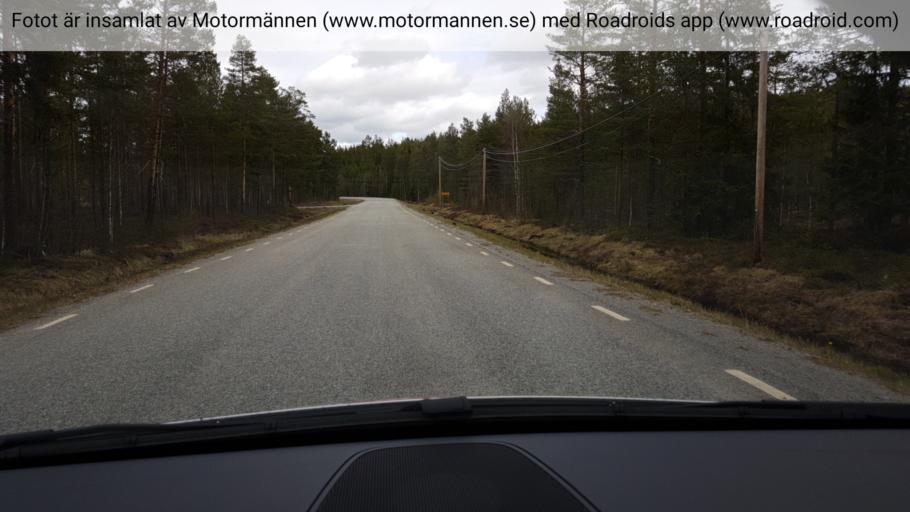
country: SE
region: Jaemtland
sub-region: Bergs Kommun
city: Hoverberg
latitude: 62.6509
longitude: 14.8128
